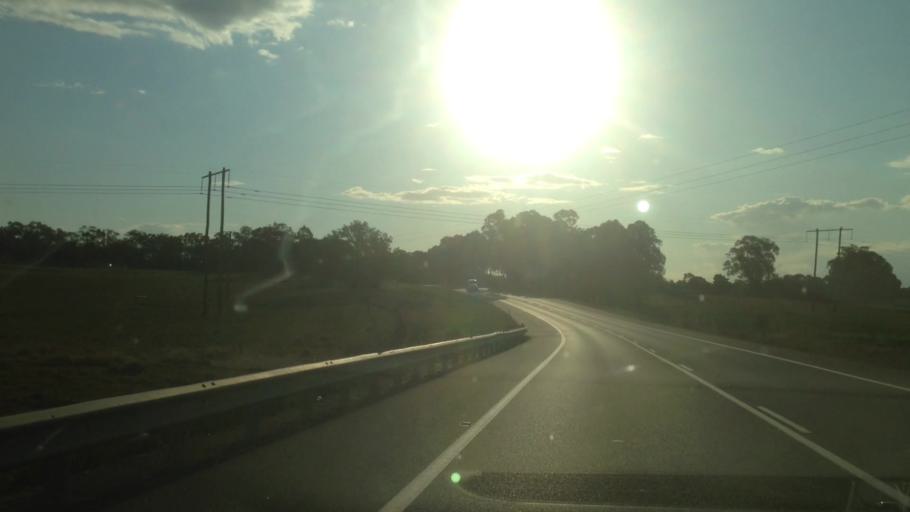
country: AU
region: New South Wales
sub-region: Cessnock
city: Heddon Greta
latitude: -32.8311
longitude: 151.5180
